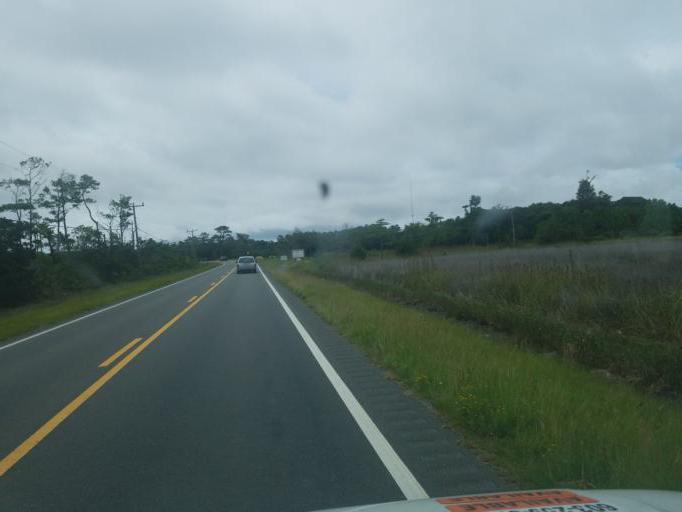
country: US
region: North Carolina
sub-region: Dare County
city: Wanchese
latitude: 35.8567
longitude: -75.6460
